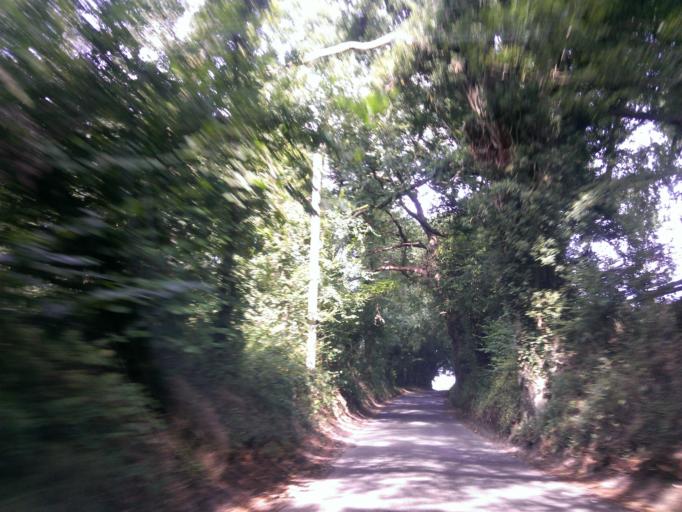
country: GB
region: England
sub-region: Essex
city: Sible Hedingham
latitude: 51.9663
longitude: 0.6244
